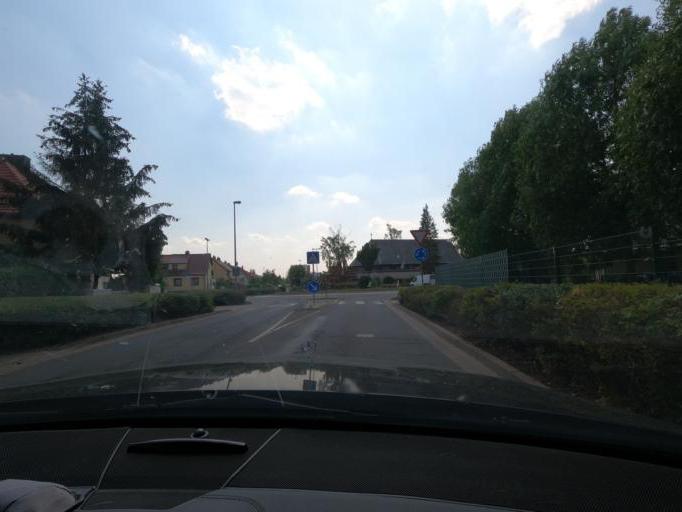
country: DE
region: Thuringia
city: Nordhausen
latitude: 51.5018
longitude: 10.7731
